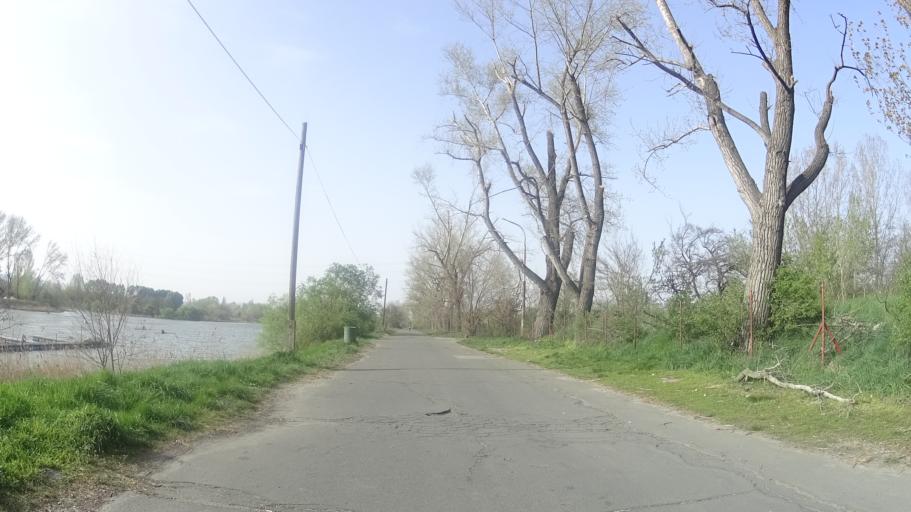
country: HU
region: Budapest
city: Budapest XX. keruelet
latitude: 47.4382
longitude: 19.0892
